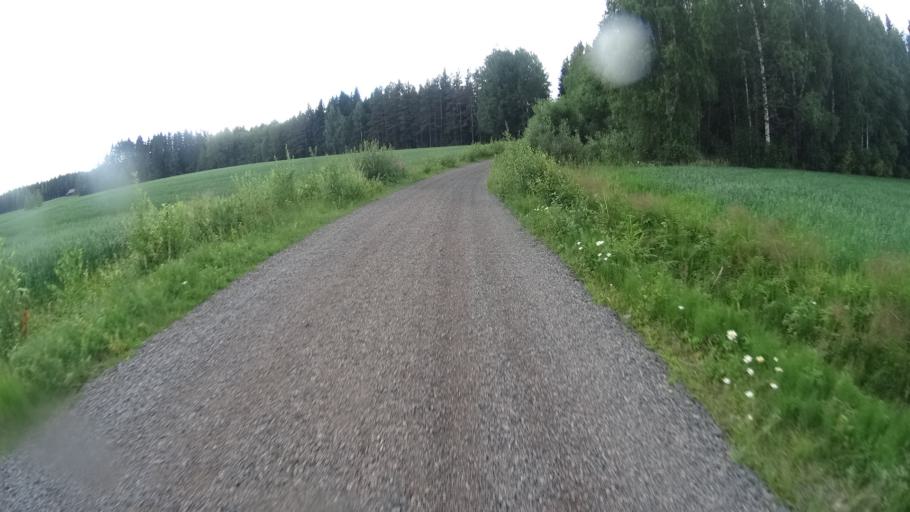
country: FI
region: Uusimaa
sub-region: Helsinki
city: Karkkila
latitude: 60.5944
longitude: 24.1636
